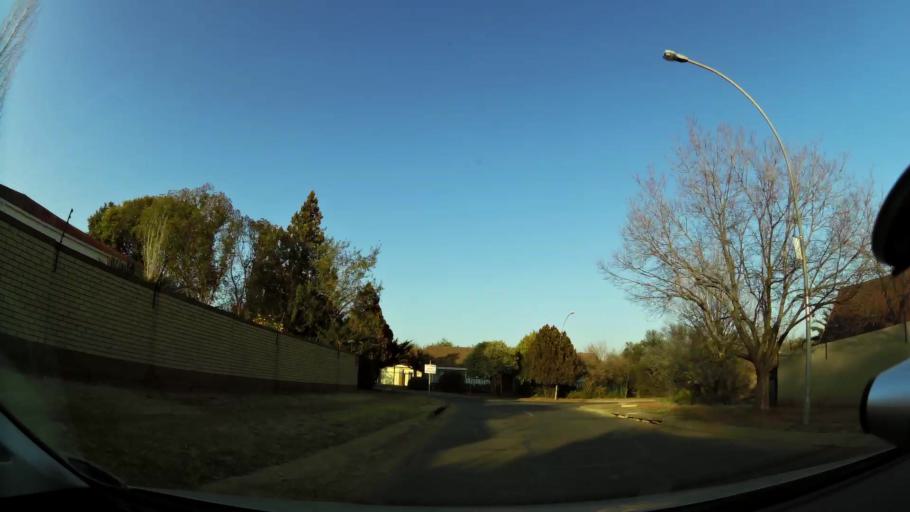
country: ZA
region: Orange Free State
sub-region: Mangaung Metropolitan Municipality
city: Bloemfontein
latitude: -29.0931
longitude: 26.1520
